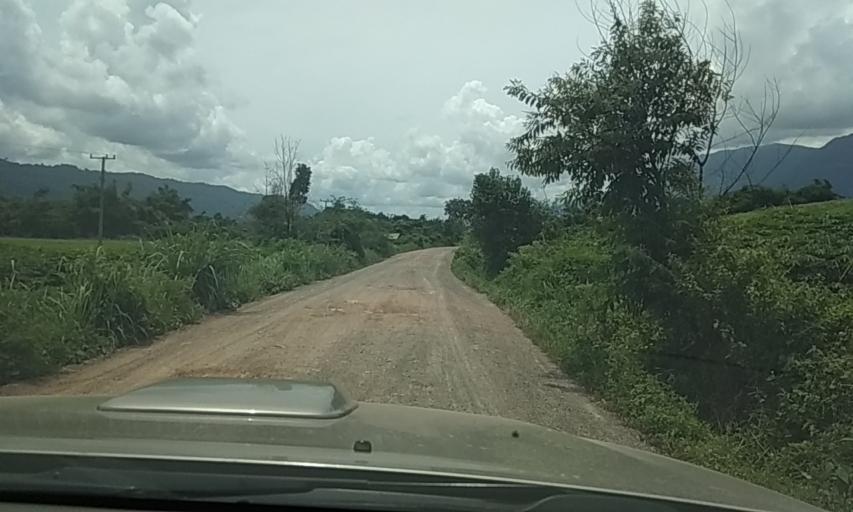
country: LA
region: Bolikhamxai
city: Ban Nahin
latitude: 18.1462
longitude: 104.7491
